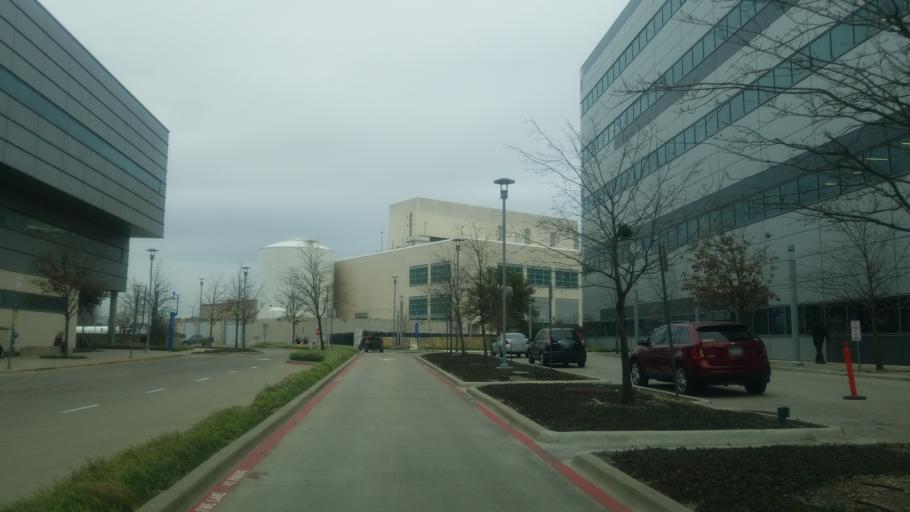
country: US
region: Texas
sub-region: Dallas County
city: Dallas
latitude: 32.8133
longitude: -96.8342
